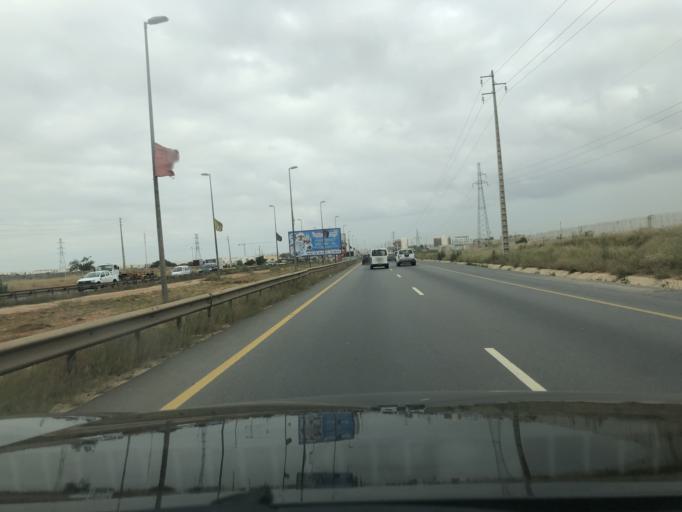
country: AO
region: Luanda
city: Luanda
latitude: -8.9737
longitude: 13.2274
